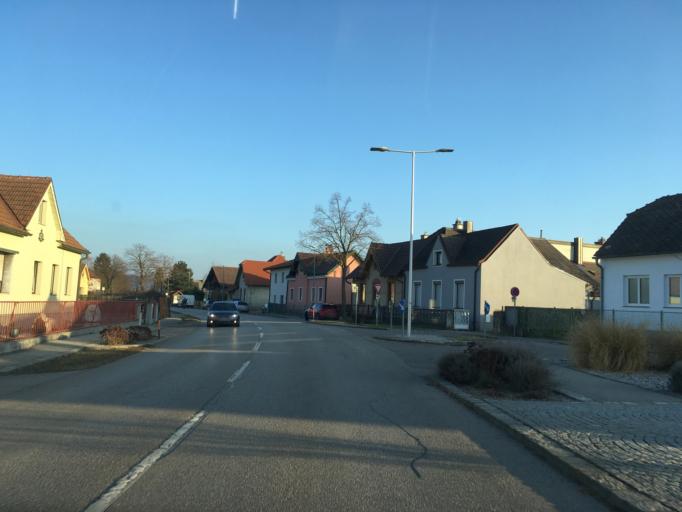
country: AT
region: Lower Austria
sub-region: Politischer Bezirk Tulln
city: Konigstetten
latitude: 48.3312
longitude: 16.1575
